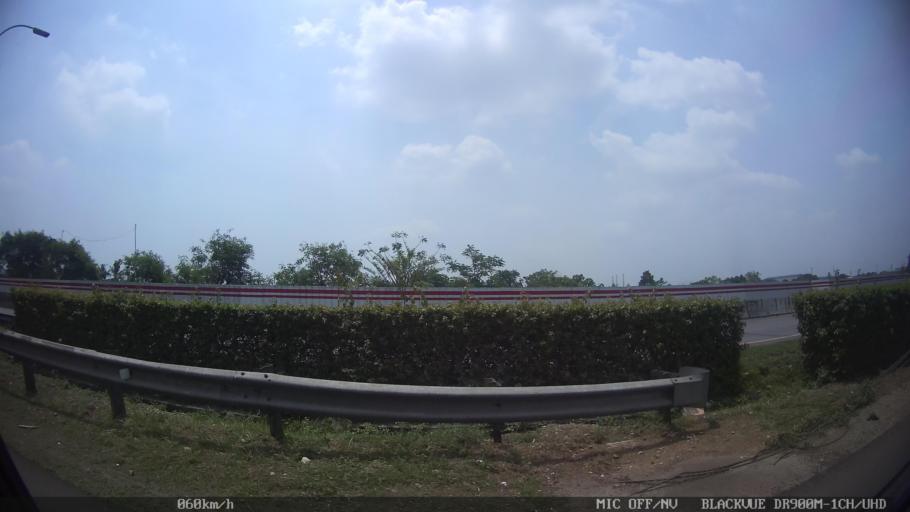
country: ID
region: West Java
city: Kresek
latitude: -6.1434
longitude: 106.2828
